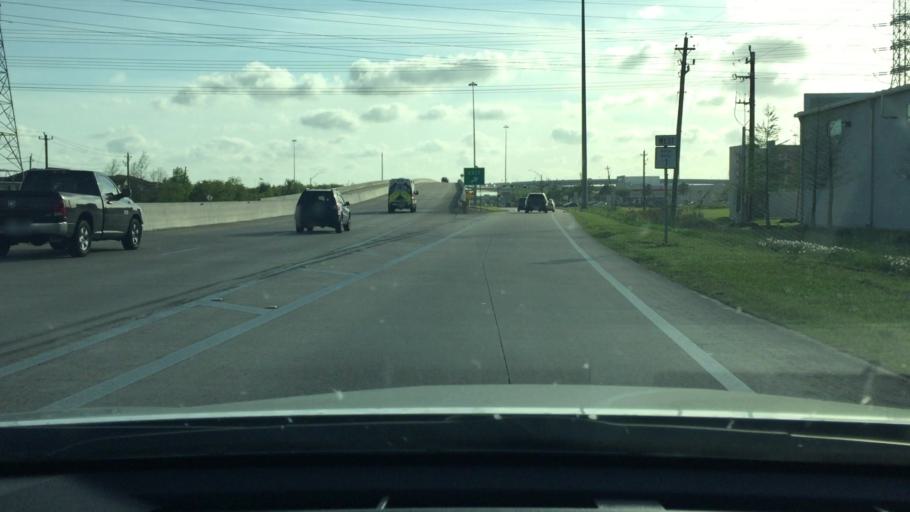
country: US
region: Texas
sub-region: Harris County
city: Webster
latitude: 29.5254
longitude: -95.1186
